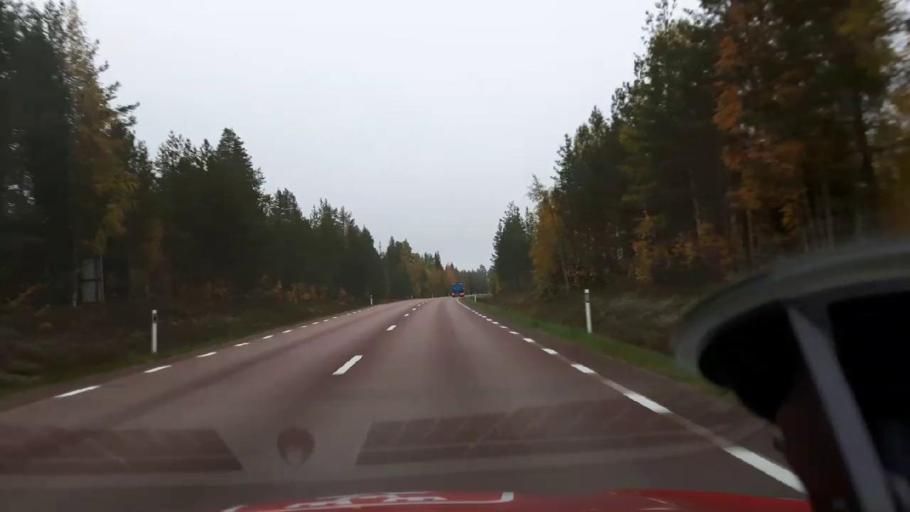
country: SE
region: Jaemtland
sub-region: Bergs Kommun
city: Hoverberg
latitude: 62.6022
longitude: 14.4130
